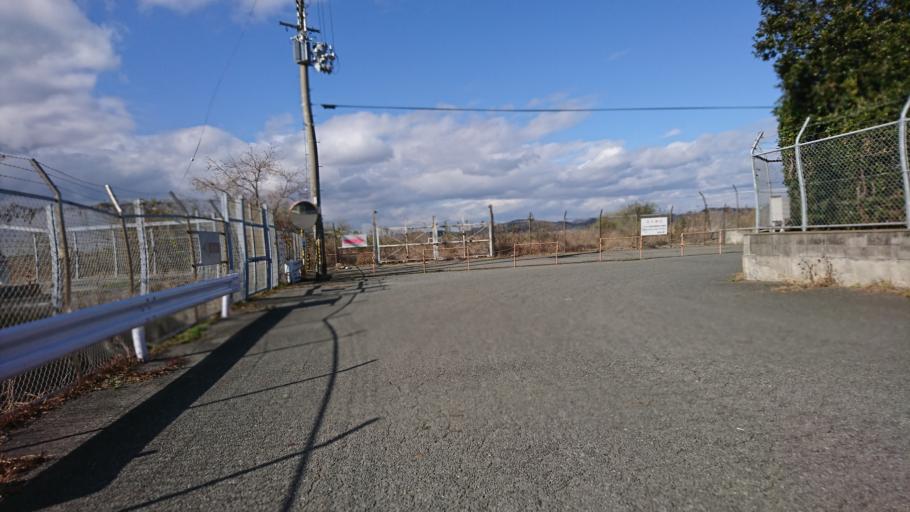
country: JP
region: Hyogo
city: Shirahamacho-usazakiminami
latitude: 34.7514
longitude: 134.7639
